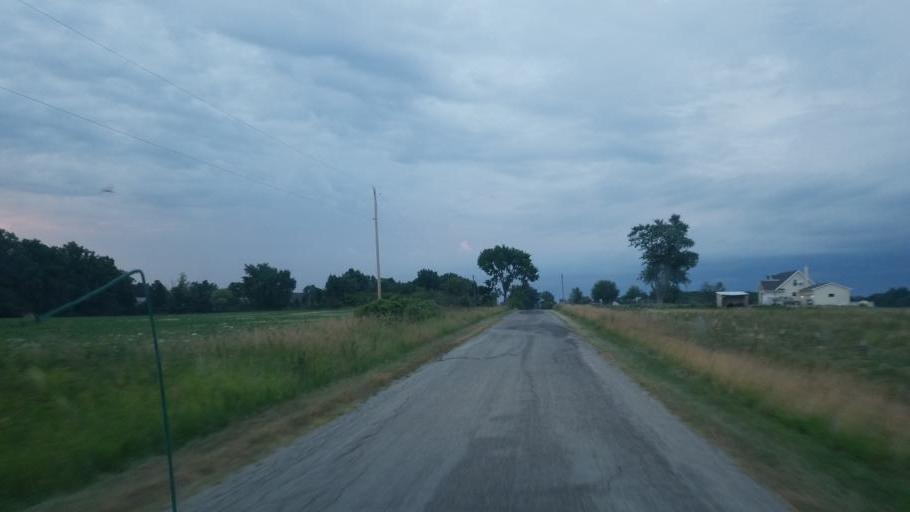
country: US
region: Ohio
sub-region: Defiance County
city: Hicksville
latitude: 41.3310
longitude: -84.8302
